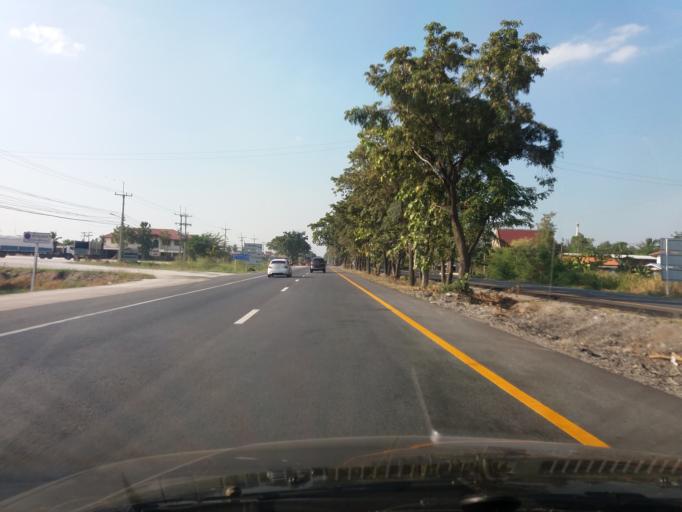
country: TH
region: Nakhon Sawan
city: Banphot Phisai
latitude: 15.8193
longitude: 99.9410
